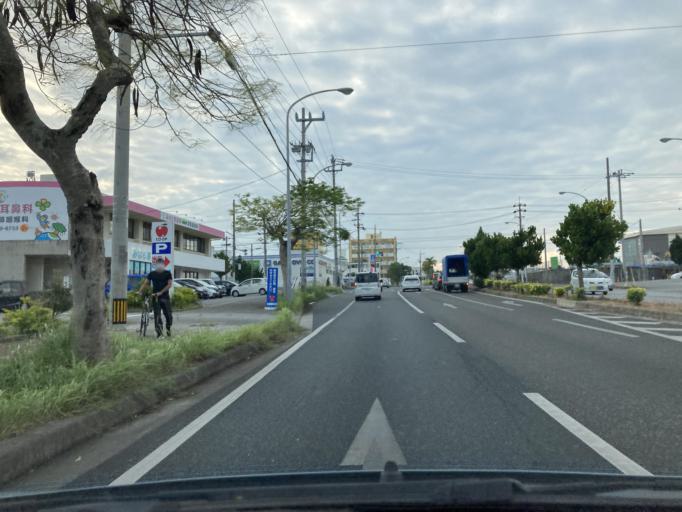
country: JP
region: Okinawa
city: Okinawa
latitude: 26.3522
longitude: 127.8184
